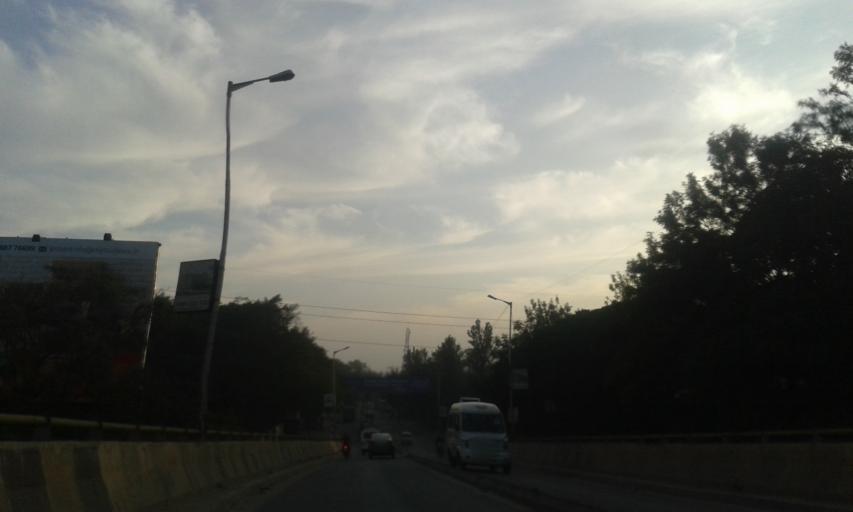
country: IN
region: Karnataka
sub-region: Bangalore Rural
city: Hoskote
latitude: 12.9957
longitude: 77.7583
